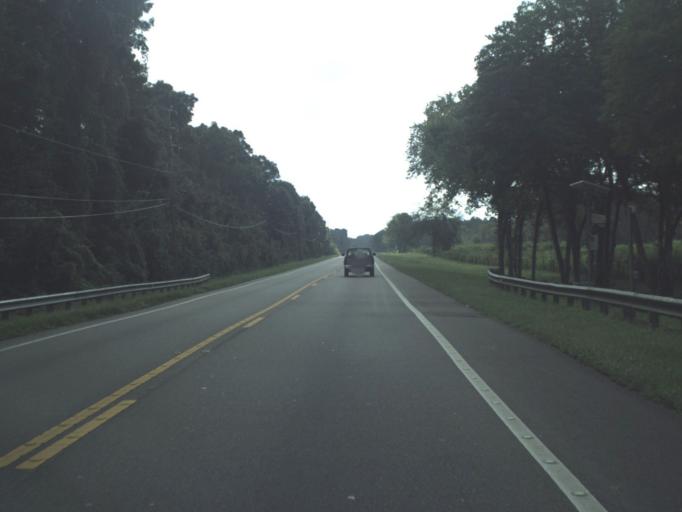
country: US
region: Florida
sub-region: Pasco County
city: Shady Hills
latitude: 28.3293
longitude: -82.5366
